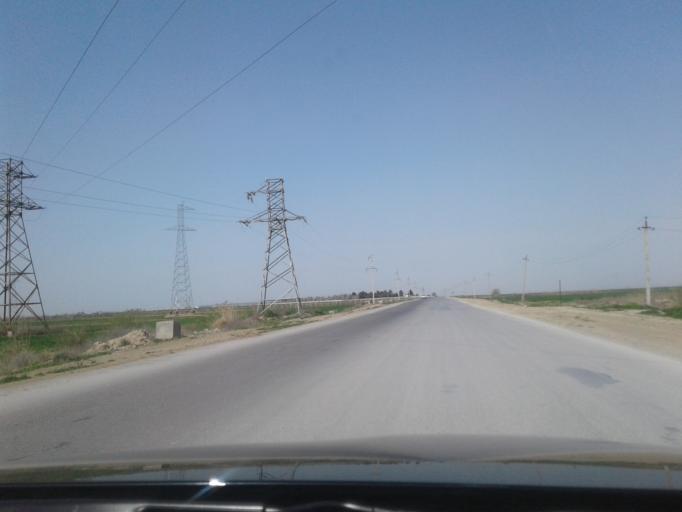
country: TM
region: Ahal
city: Abadan
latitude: 38.1801
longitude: 57.9777
